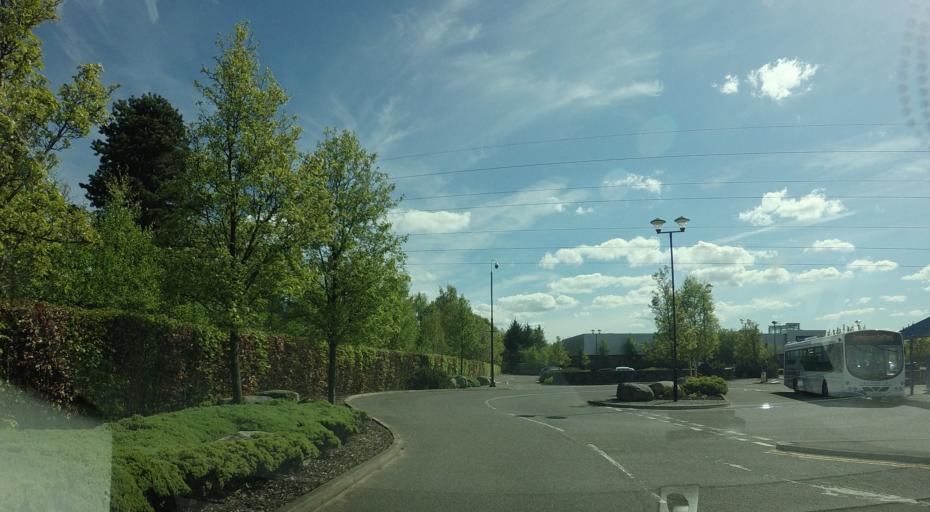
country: GB
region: Scotland
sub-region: Stirling
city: Bannockburn
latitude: 56.1150
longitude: -3.9069
